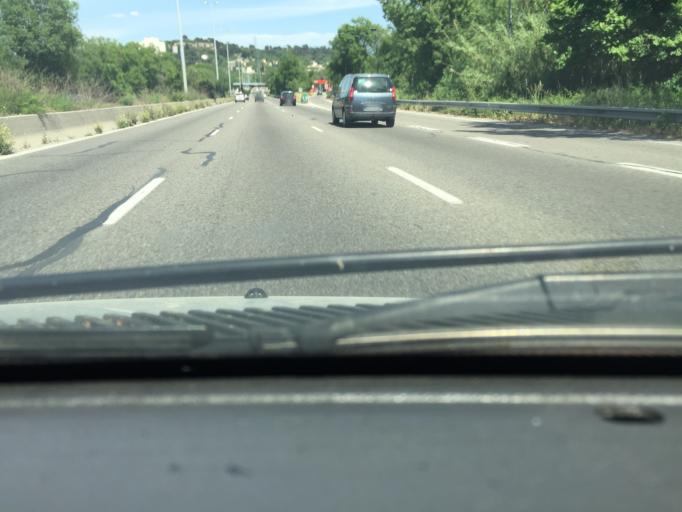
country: FR
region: Provence-Alpes-Cote d'Azur
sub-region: Departement des Bouches-du-Rhone
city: Marseille 11
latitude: 43.2909
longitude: 5.4498
